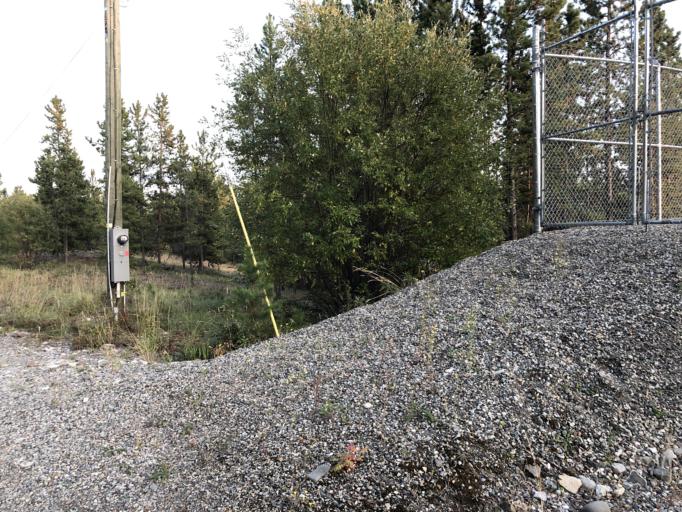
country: CA
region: Yukon
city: Whitehorse
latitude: 60.8812
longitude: -135.3631
